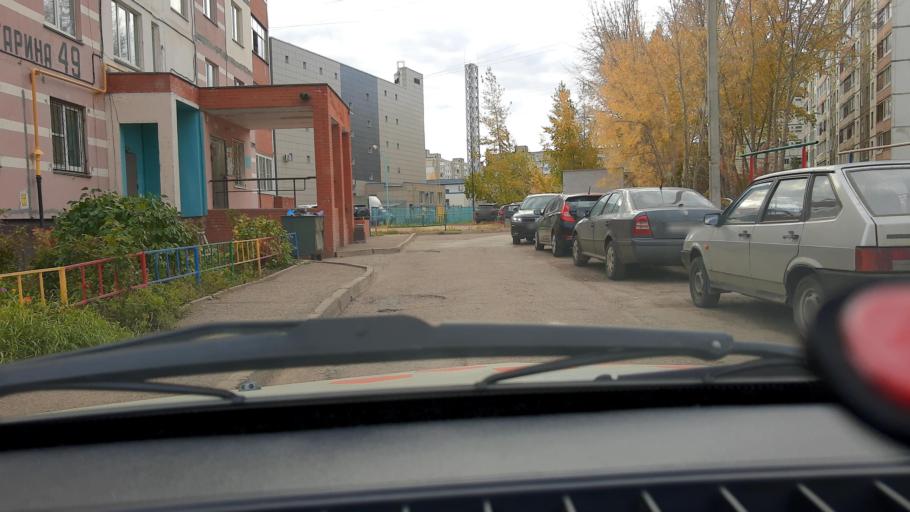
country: RU
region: Bashkortostan
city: Ufa
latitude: 54.7758
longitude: 56.0758
